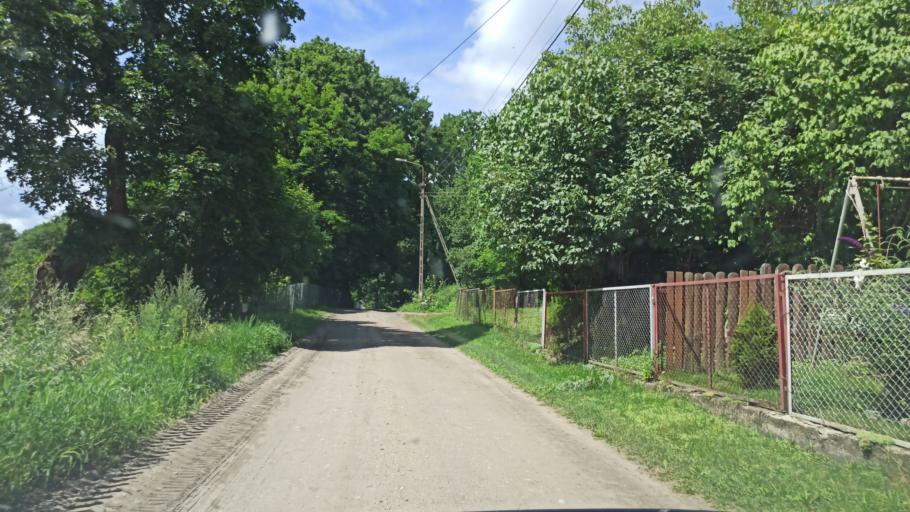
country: PL
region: Warmian-Masurian Voivodeship
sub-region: Powiat ostrodzki
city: Milakowo
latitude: 53.8604
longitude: 20.0642
